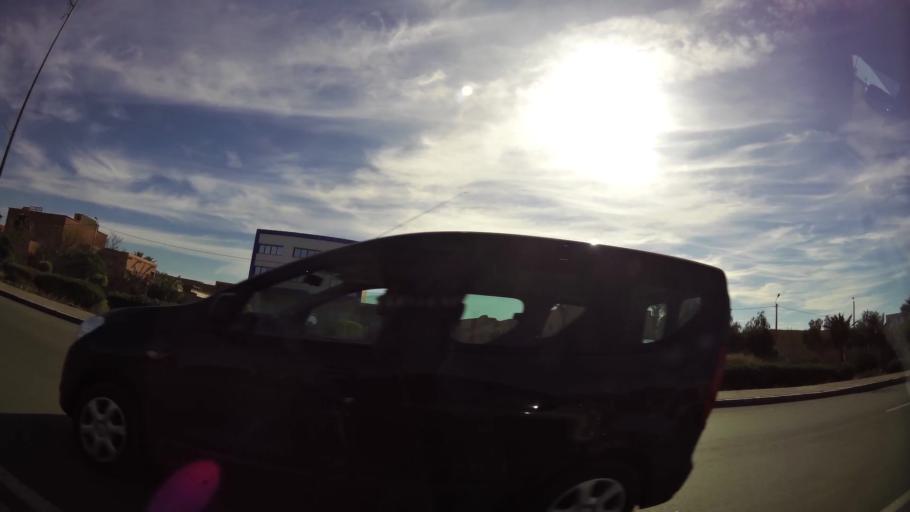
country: MA
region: Marrakech-Tensift-Al Haouz
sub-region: Marrakech
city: Marrakesh
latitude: 31.6796
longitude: -8.0484
